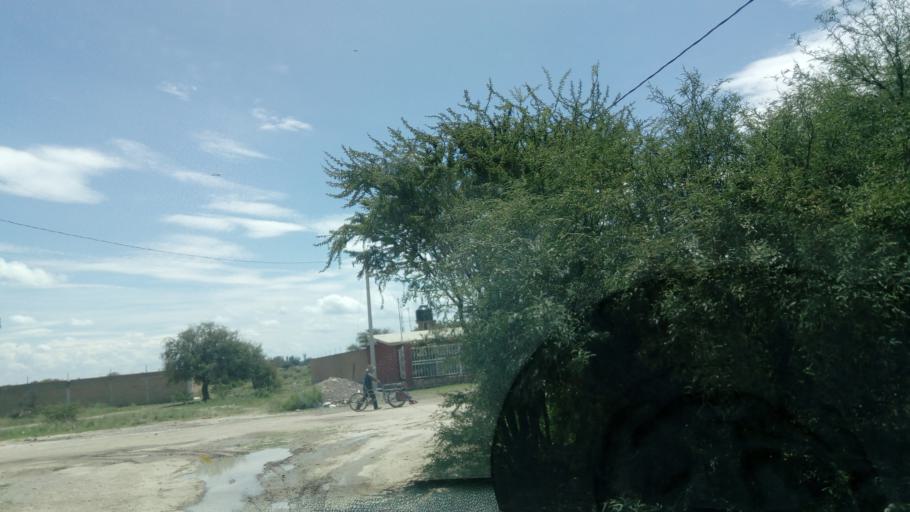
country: MX
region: Durango
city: Victoria de Durango
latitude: 24.0161
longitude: -104.5882
